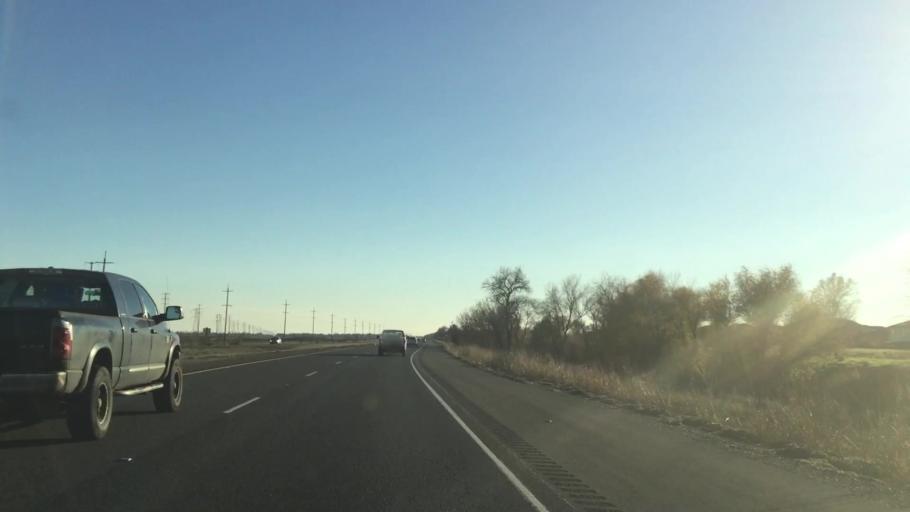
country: US
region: California
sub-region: Yuba County
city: Plumas Lake
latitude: 39.0118
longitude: -121.5435
